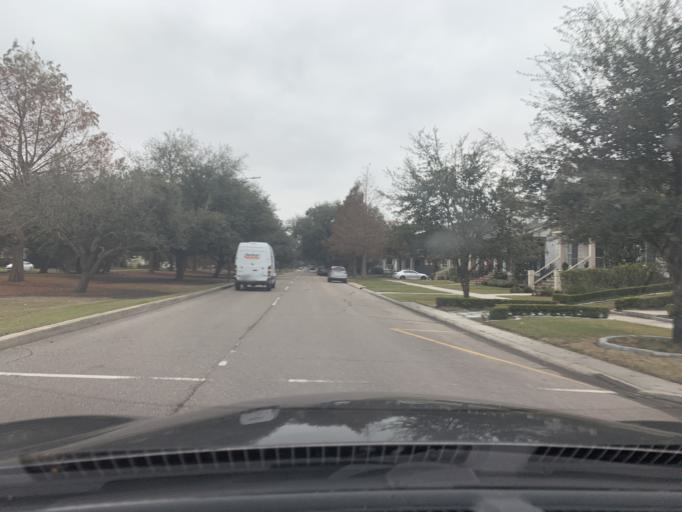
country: US
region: Louisiana
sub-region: Jefferson Parish
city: Metairie
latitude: 30.0159
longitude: -90.1069
